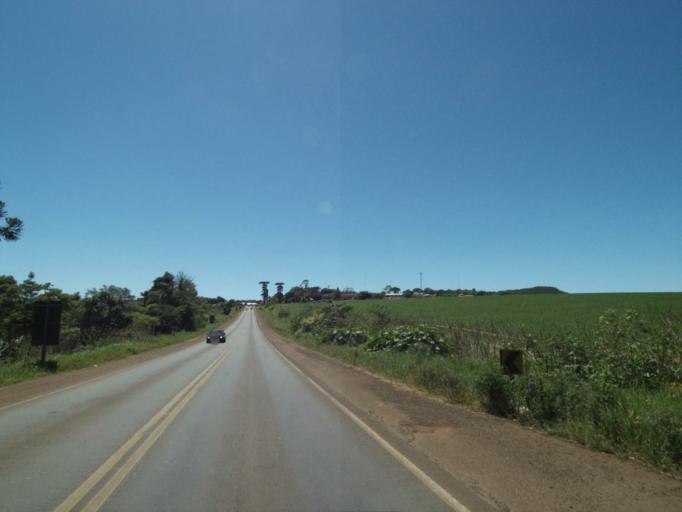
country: BR
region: Parana
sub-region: Pato Branco
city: Pato Branco
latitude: -26.2566
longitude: -52.7798
